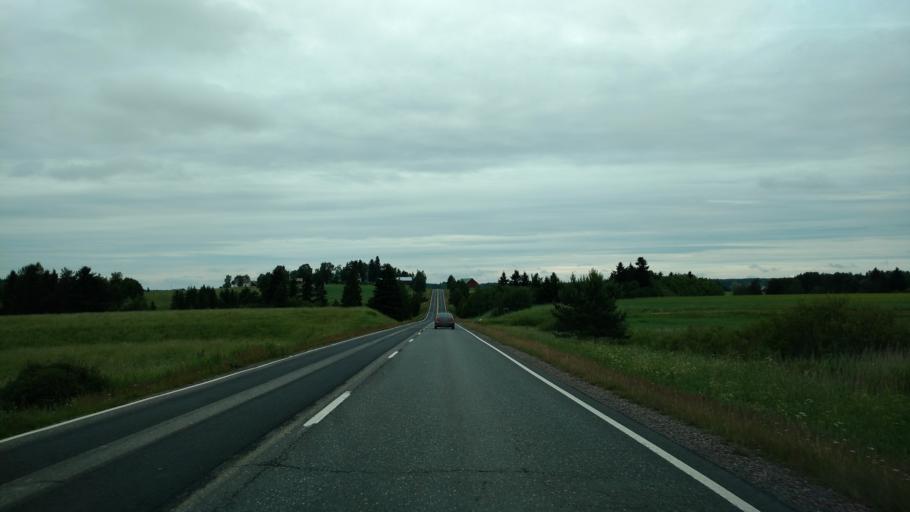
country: FI
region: Varsinais-Suomi
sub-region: Salo
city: Halikko
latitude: 60.4691
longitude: 23.0158
